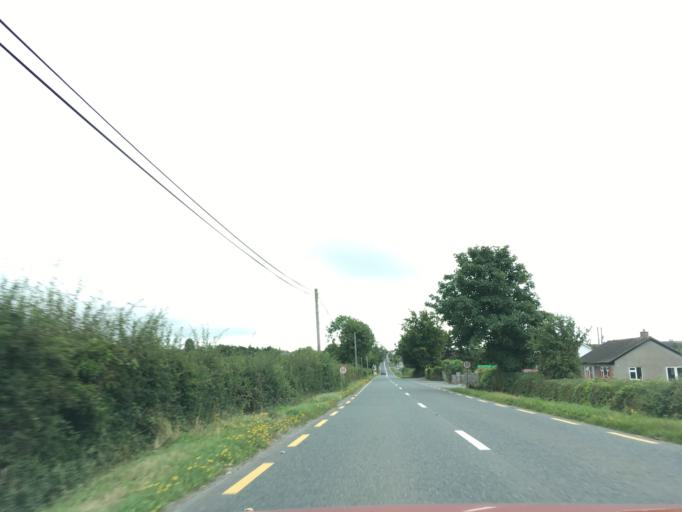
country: IE
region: Munster
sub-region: South Tipperary
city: Cluain Meala
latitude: 52.4162
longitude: -7.7600
